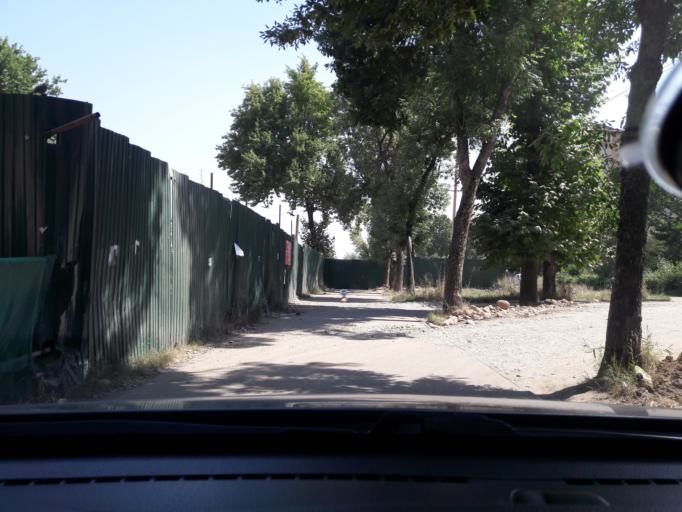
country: TJ
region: Dushanbe
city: Dushanbe
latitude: 38.5880
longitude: 68.7551
